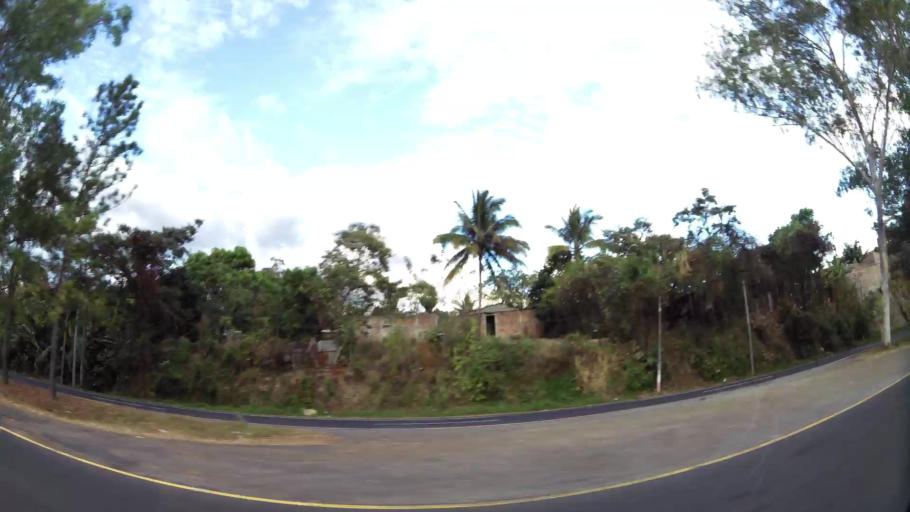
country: SV
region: San Vicente
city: San Sebastian
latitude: 13.7200
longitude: -88.8592
